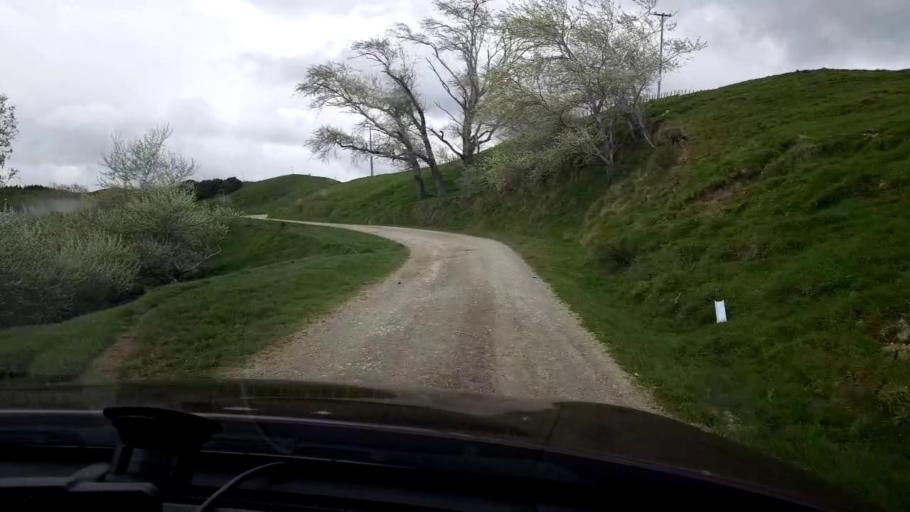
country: NZ
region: Gisborne
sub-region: Gisborne District
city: Gisborne
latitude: -38.3662
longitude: 177.9564
